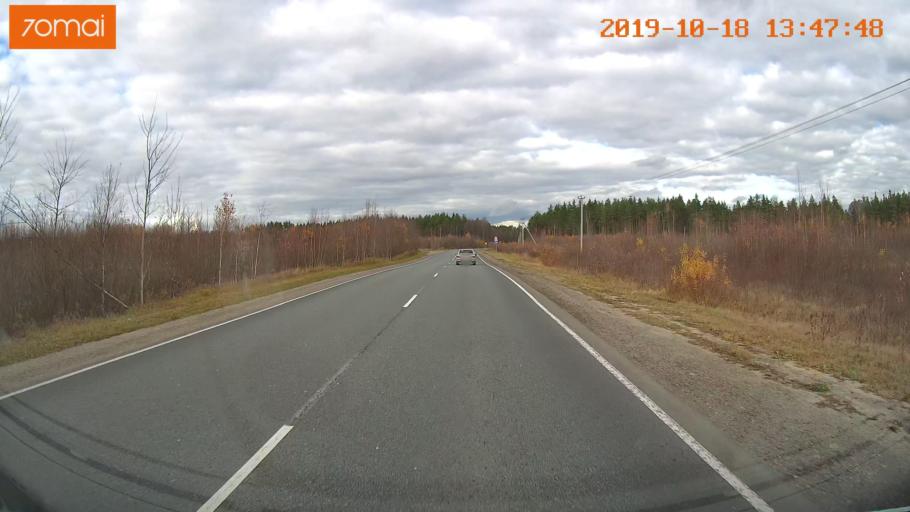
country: RU
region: Moskovskaya
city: Radovitskiy
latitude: 54.9802
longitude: 39.9515
